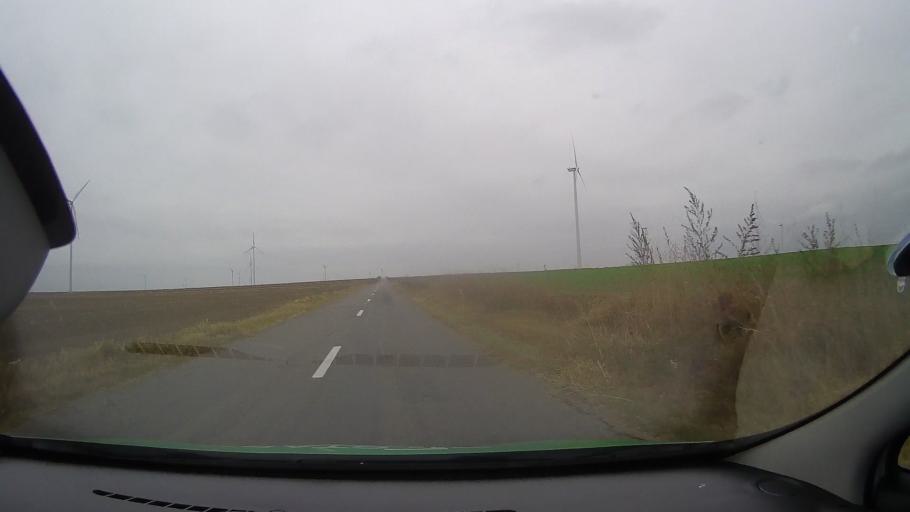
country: RO
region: Constanta
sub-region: Comuna Pantelimon
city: Pantelimon
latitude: 44.5046
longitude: 28.3482
